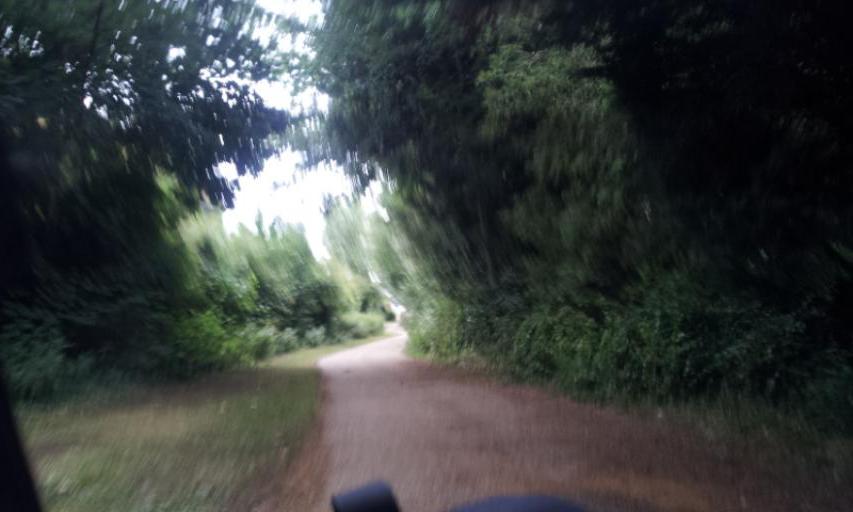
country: GB
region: England
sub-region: Kent
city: Herne Bay
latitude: 51.3729
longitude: 1.1683
